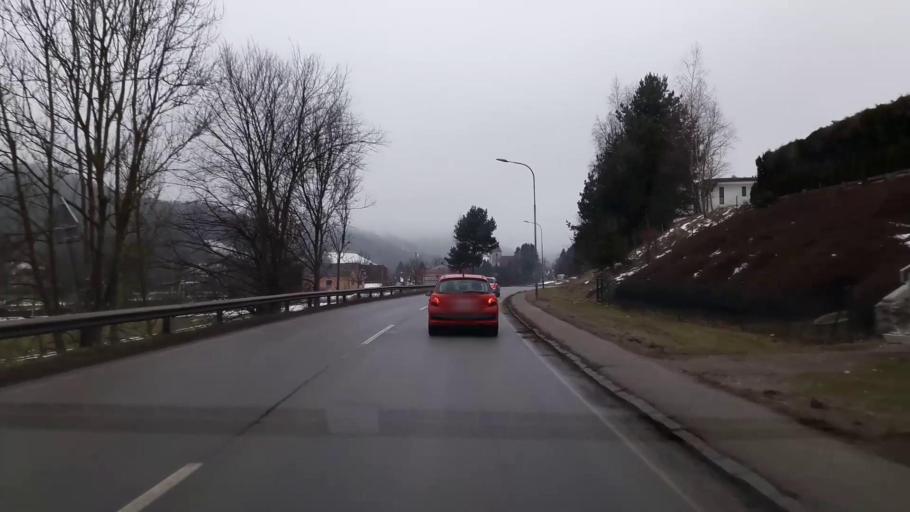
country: AT
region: Lower Austria
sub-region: Politischer Bezirk Neunkirchen
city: Edlitz
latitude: 47.5757
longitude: 16.0996
